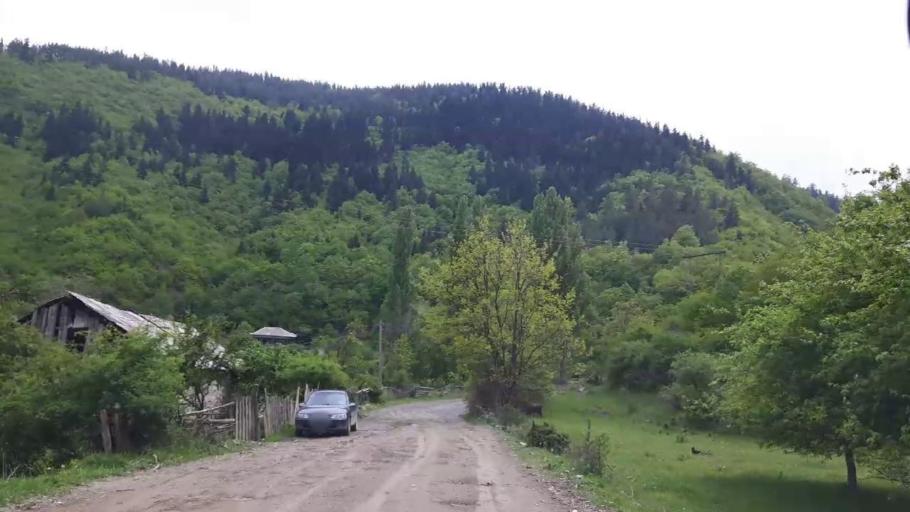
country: GE
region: Shida Kartli
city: Gori
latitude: 41.8844
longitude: 43.9978
